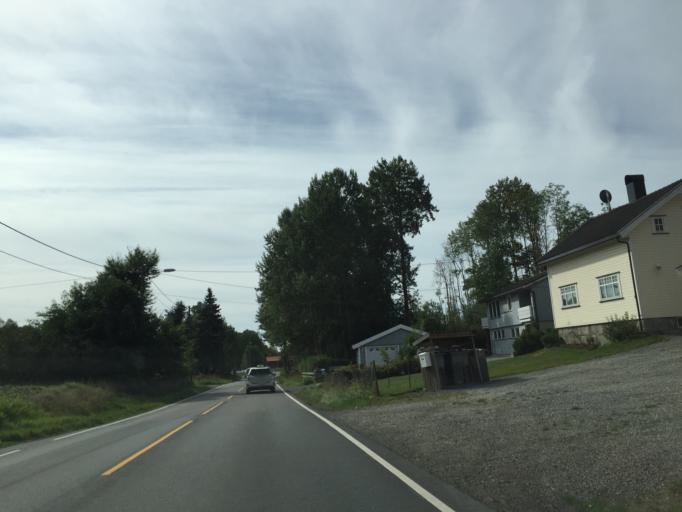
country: NO
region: Ostfold
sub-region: Moss
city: Moss
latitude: 59.4844
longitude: 10.6972
